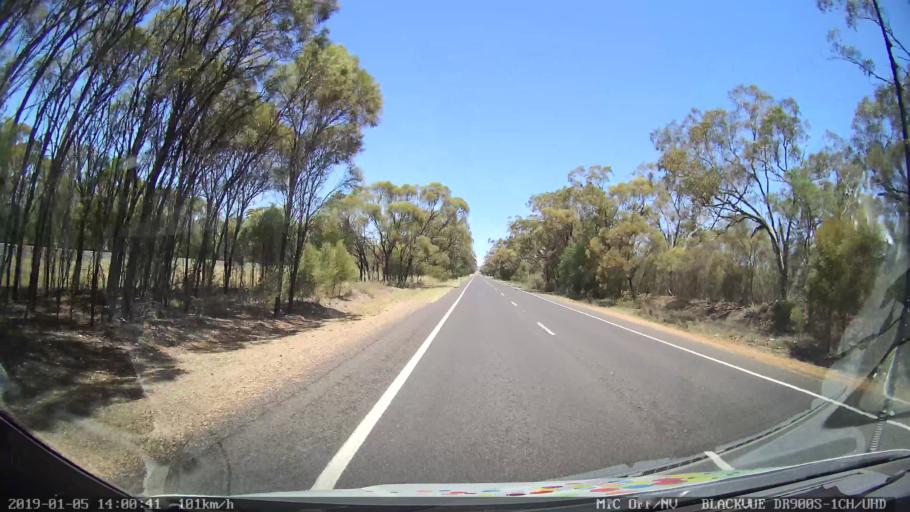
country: AU
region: New South Wales
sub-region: Gunnedah
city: Gunnedah
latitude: -31.1620
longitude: 150.3153
